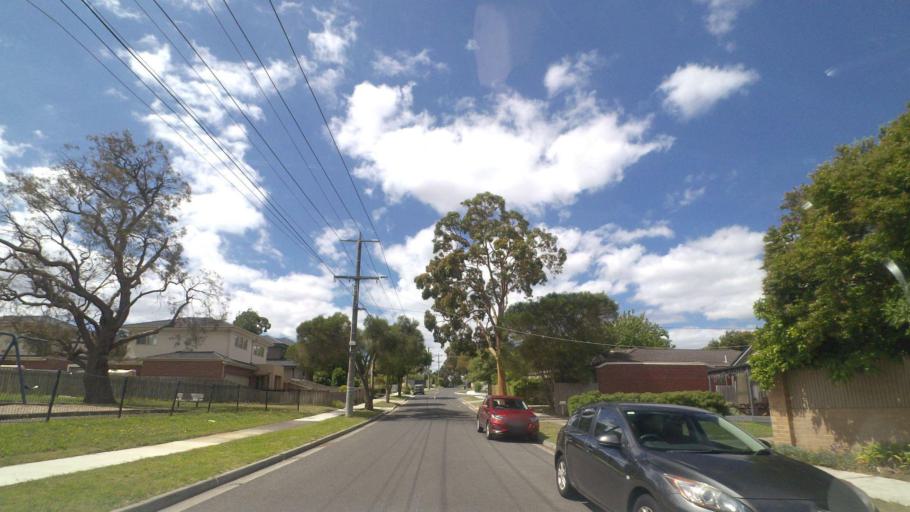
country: AU
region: Victoria
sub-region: Knox
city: Bayswater
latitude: -37.8557
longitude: 145.2466
